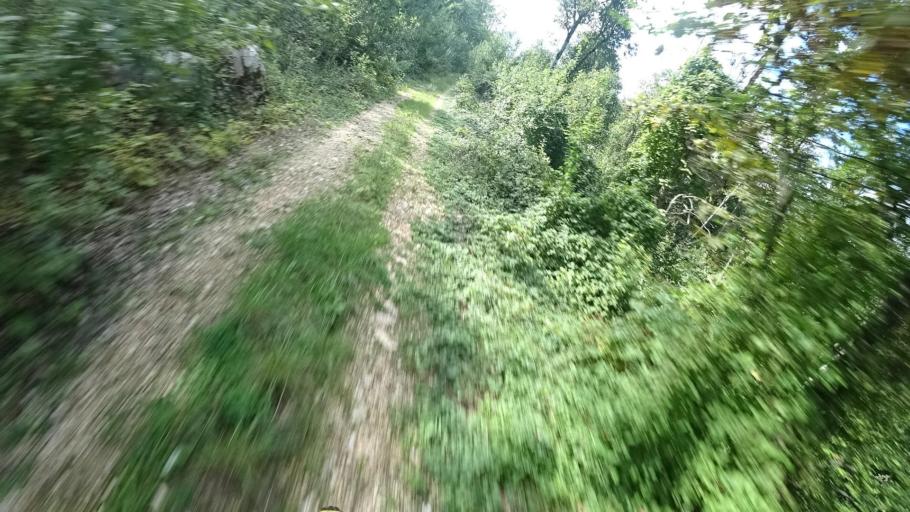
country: BA
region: Republika Srpska
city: Hiseti
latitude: 44.6622
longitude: 17.1674
